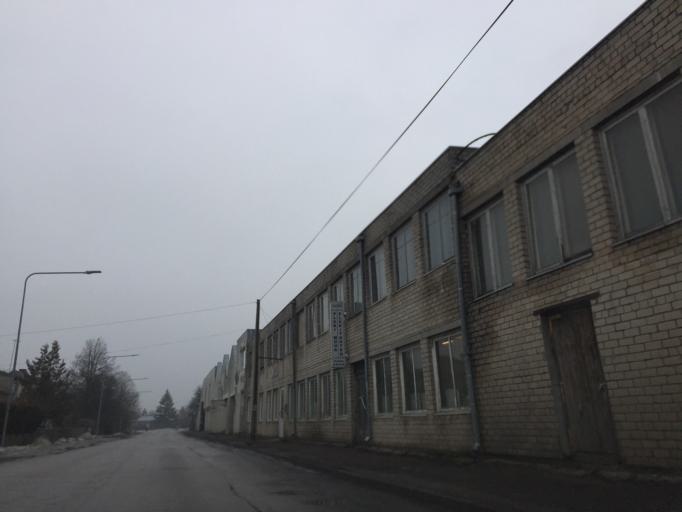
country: EE
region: Saare
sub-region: Kuressaare linn
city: Kuressaare
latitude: 58.2525
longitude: 22.4997
